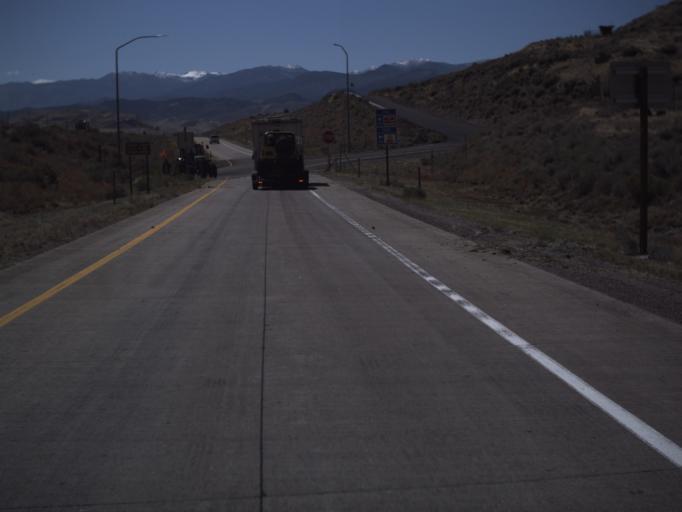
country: US
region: Utah
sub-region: Sevier County
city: Monroe
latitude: 38.6840
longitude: -112.1562
